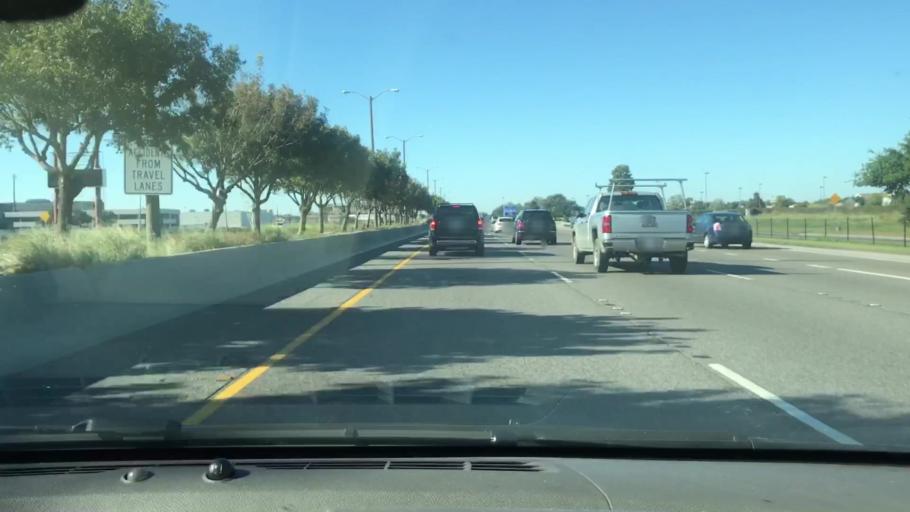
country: US
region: Louisiana
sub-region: Saint Bernard Parish
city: Arabi
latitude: 30.0357
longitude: -89.9796
